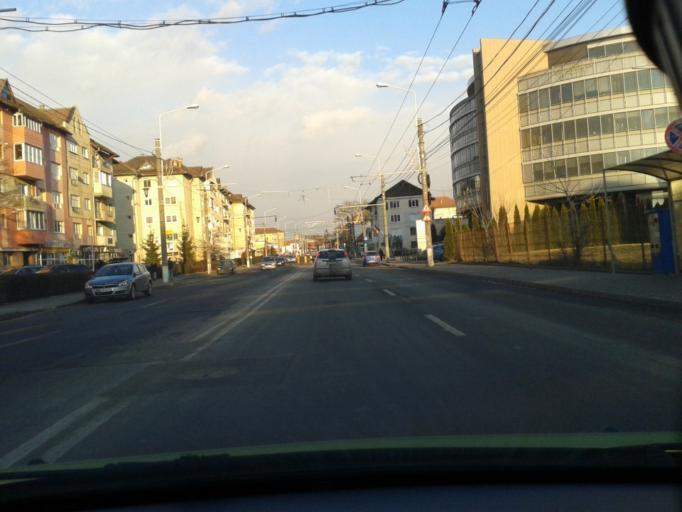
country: RO
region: Sibiu
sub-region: Municipiul Medias
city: Medias
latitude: 46.1549
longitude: 24.3393
